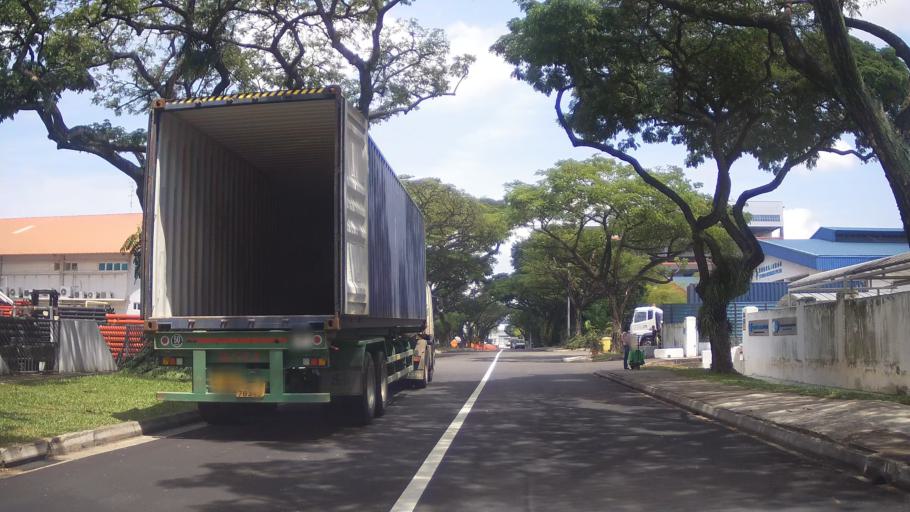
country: MY
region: Johor
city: Johor Bahru
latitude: 1.3313
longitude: 103.7146
